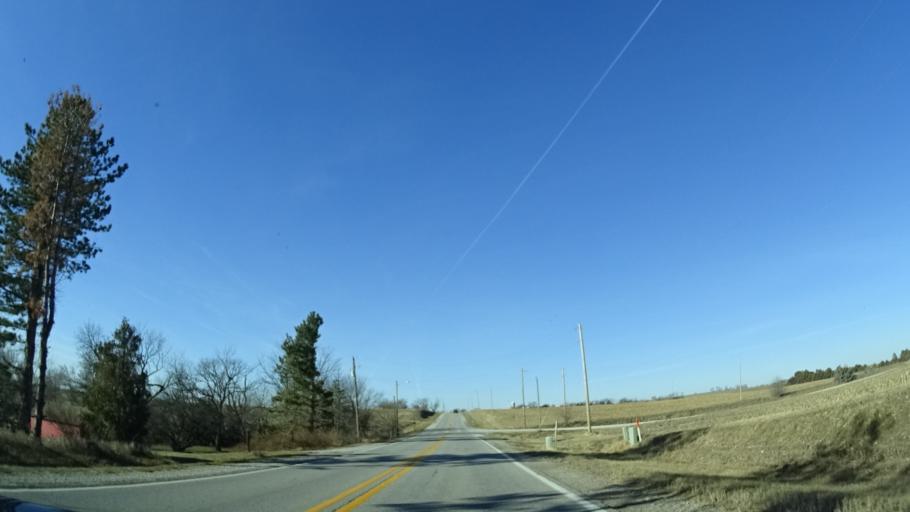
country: US
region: Nebraska
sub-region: Sarpy County
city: Papillion
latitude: 41.0891
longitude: -96.0606
